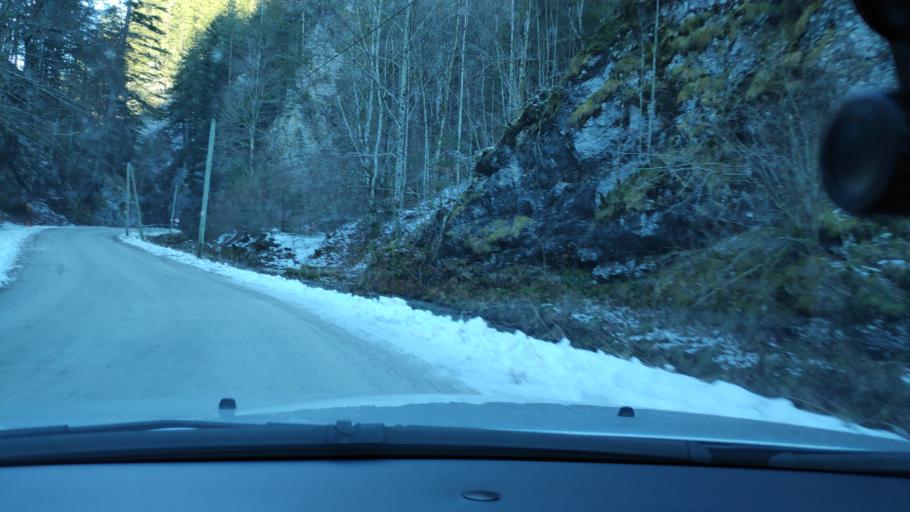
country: AT
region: Lower Austria
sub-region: Politischer Bezirk Neunkirchen
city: Schwarzau im Gebirge
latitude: 47.7567
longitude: 15.6899
